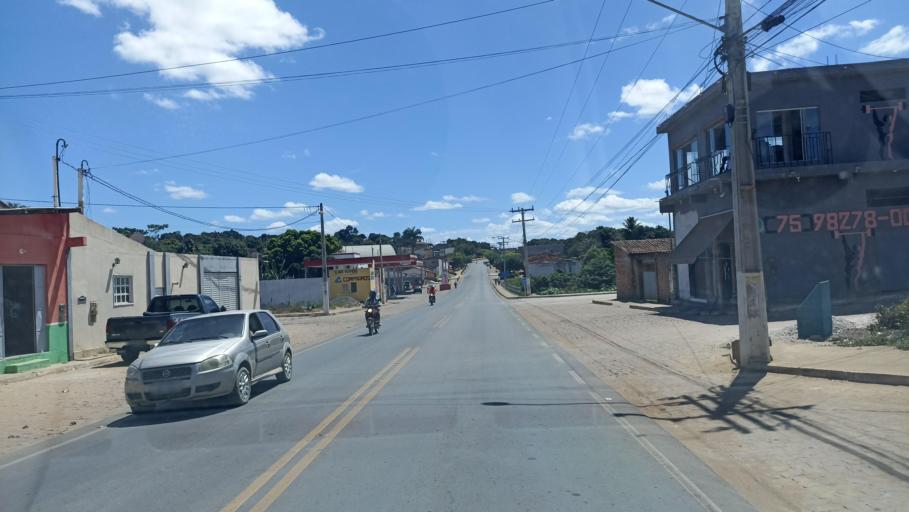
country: BR
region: Bahia
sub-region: Andarai
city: Vera Cruz
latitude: -12.7998
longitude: -41.3264
